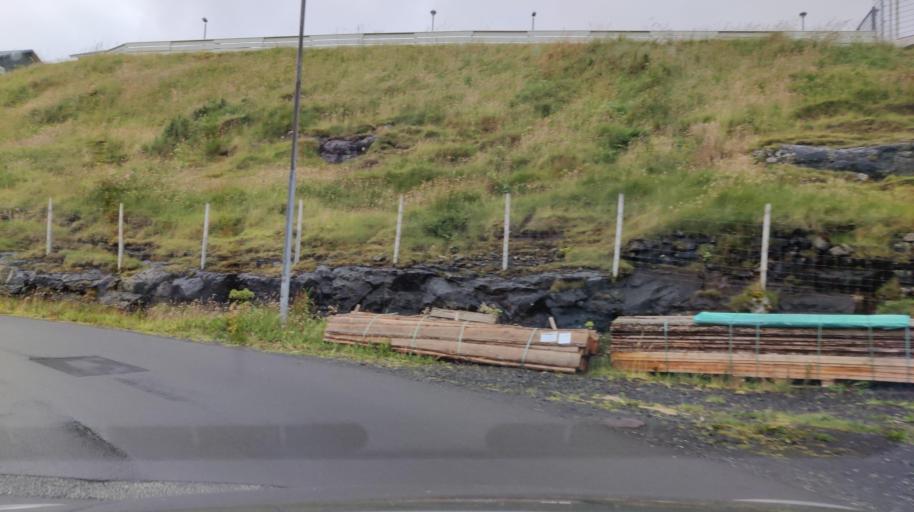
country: FO
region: Streymoy
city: Vestmanna
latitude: 62.1567
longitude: -7.1771
